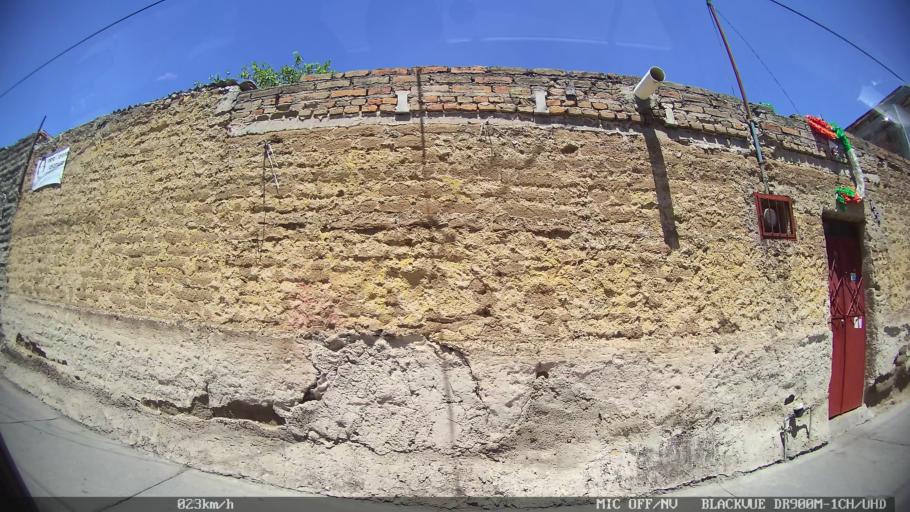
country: MX
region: Jalisco
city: Tlaquepaque
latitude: 20.6616
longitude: -103.2740
